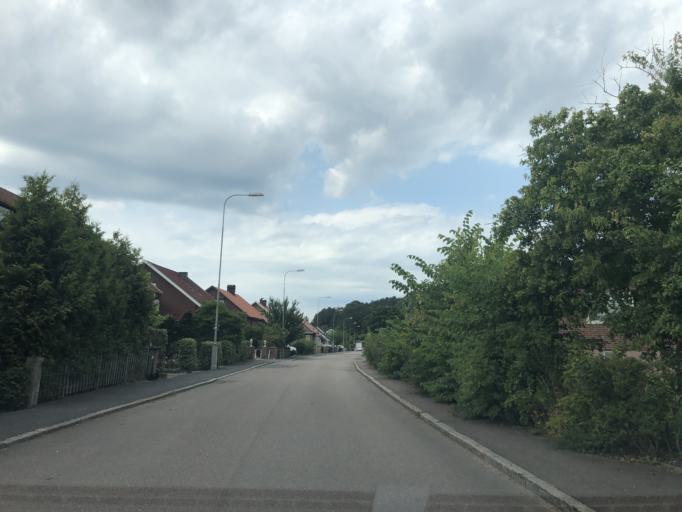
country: SE
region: Vaestra Goetaland
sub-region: Goteborg
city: Majorna
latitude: 57.7342
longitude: 11.9154
